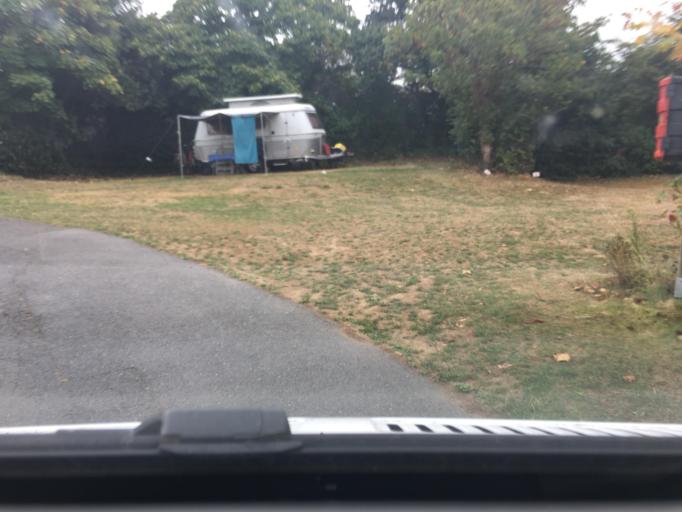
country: FR
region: Brittany
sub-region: Departement du Finistere
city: Beuzec-Cap-Sizun
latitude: 48.0832
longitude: -4.4818
